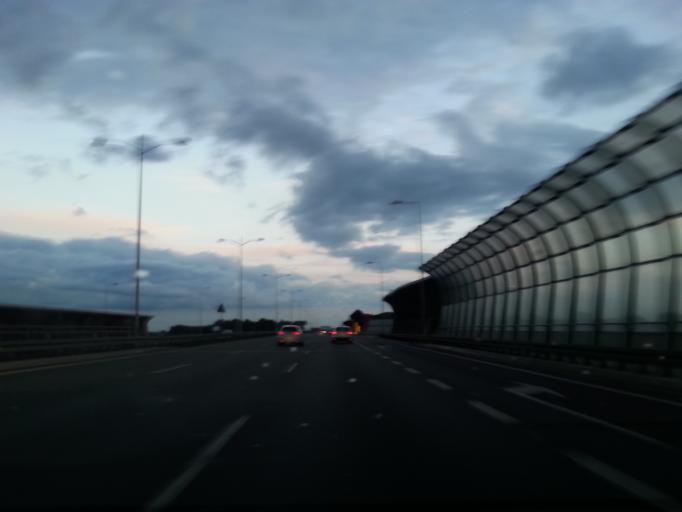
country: PL
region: Lower Silesian Voivodeship
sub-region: Powiat wroclawski
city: Smolec
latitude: 51.0670
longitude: 16.9286
